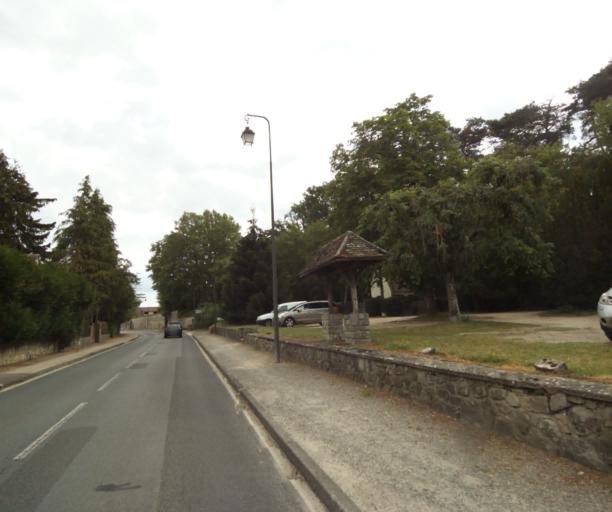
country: FR
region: Ile-de-France
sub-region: Departement de Seine-et-Marne
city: Arbonne-la-Foret
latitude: 48.4104
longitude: 2.5643
